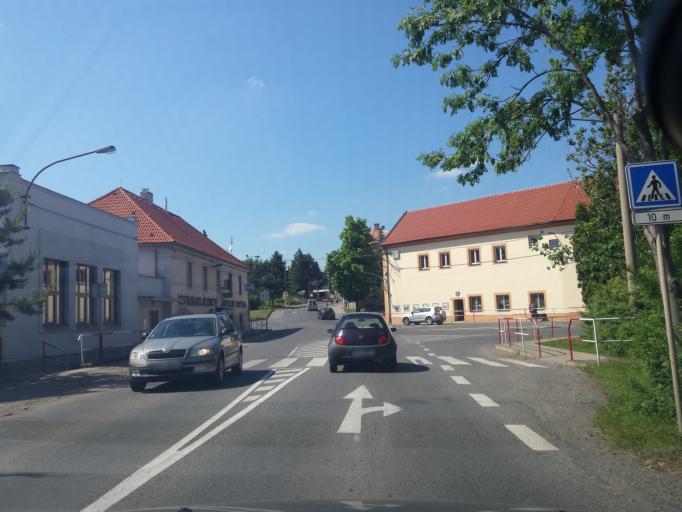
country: CZ
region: Central Bohemia
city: Velke Prilepy
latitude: 50.1601
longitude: 14.3123
